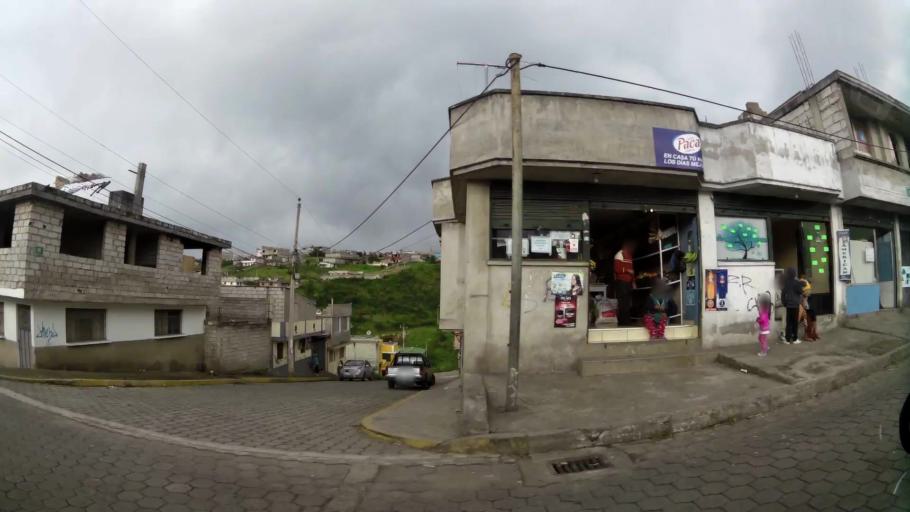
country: EC
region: Pichincha
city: Quito
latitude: -0.2985
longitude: -78.5245
